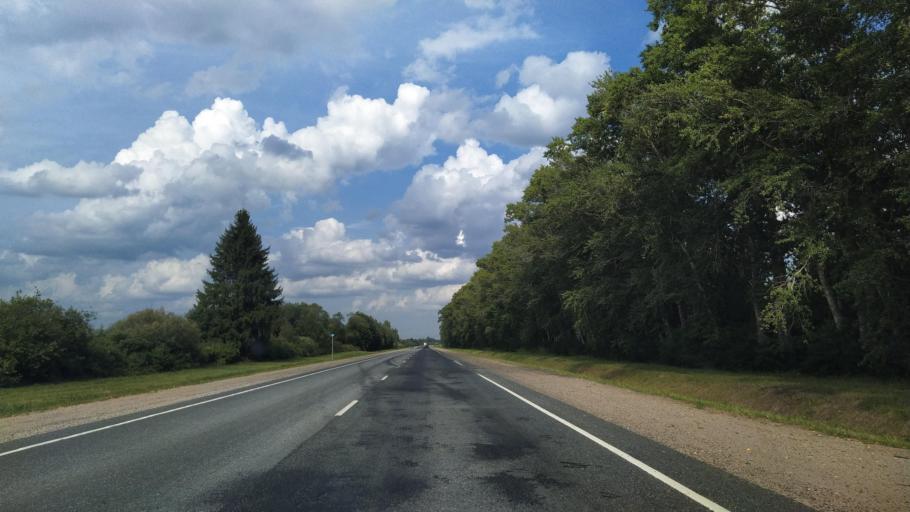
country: RU
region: Novgorod
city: Shimsk
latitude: 58.1921
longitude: 30.5684
